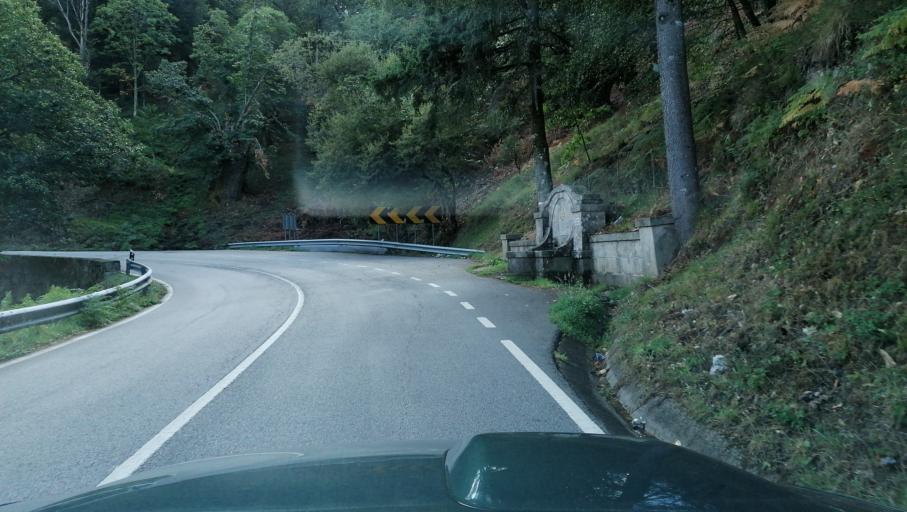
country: PT
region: Vila Real
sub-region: Vila Pouca de Aguiar
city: Vila Pouca de Aguiar
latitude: 41.5063
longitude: -7.6244
